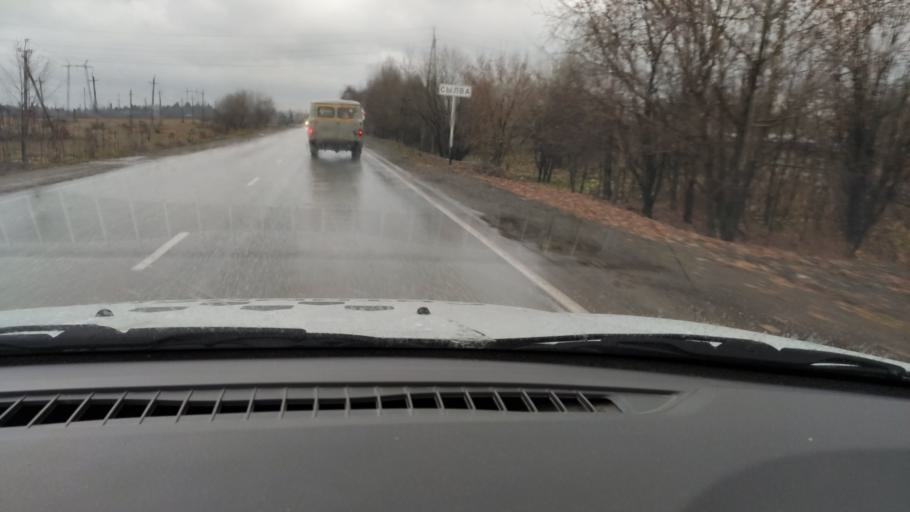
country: RU
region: Perm
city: Sylva
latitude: 58.0282
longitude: 56.7121
